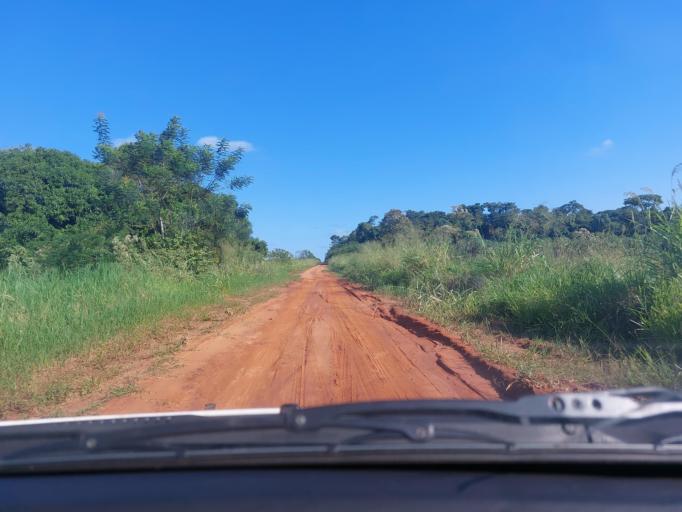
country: PY
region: San Pedro
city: Guayaybi
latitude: -24.5025
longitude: -56.5459
